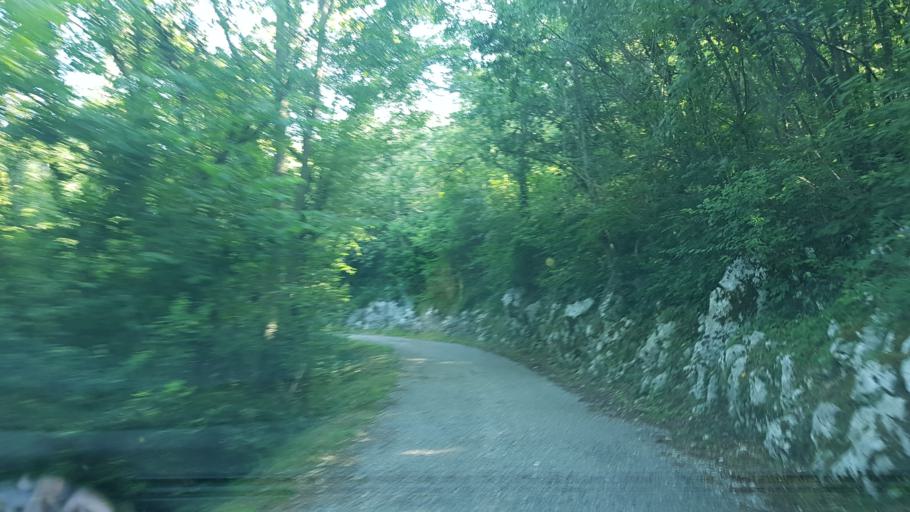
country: IT
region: Friuli Venezia Giulia
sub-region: Provincia di Udine
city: Nimis
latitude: 46.2294
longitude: 13.2549
